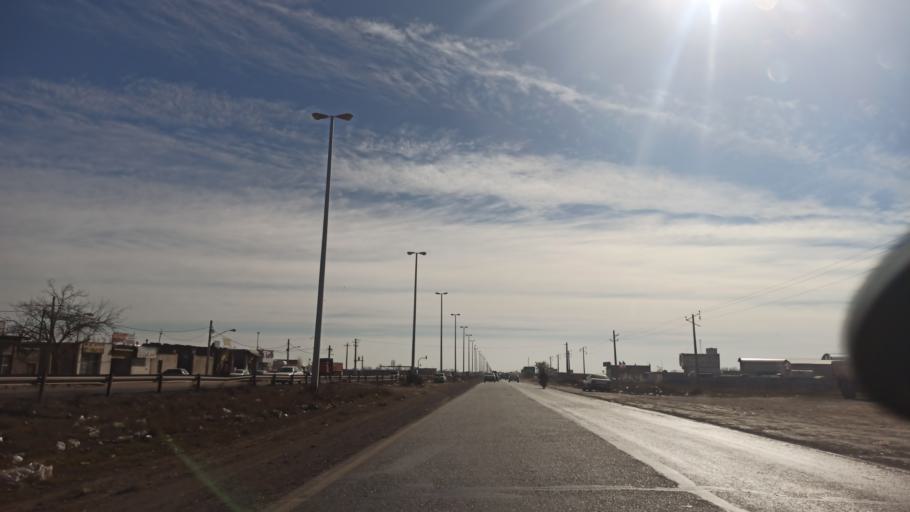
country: IR
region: Qazvin
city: Alvand
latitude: 36.2062
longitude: 50.0128
